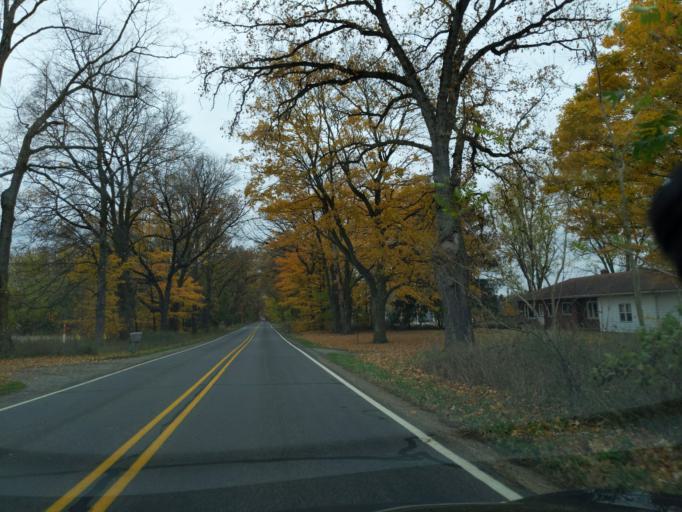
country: US
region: Michigan
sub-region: Jackson County
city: Spring Arbor
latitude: 42.2887
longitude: -84.6001
